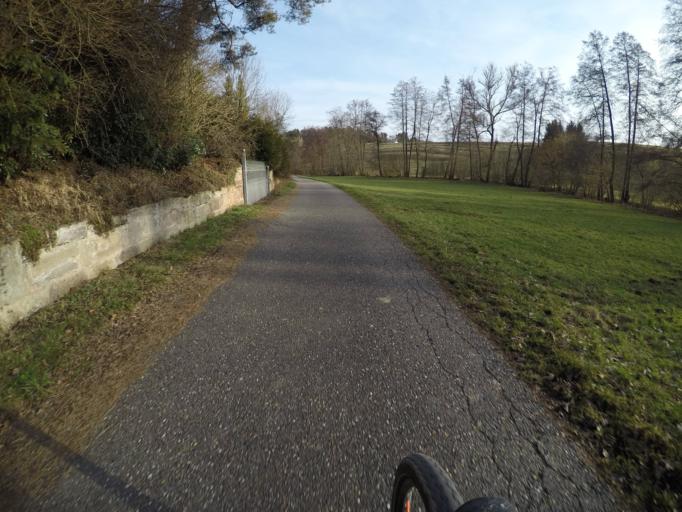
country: DE
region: Baden-Wuerttemberg
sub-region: Regierungsbezirk Stuttgart
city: Schonaich
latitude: 48.6511
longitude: 9.0521
